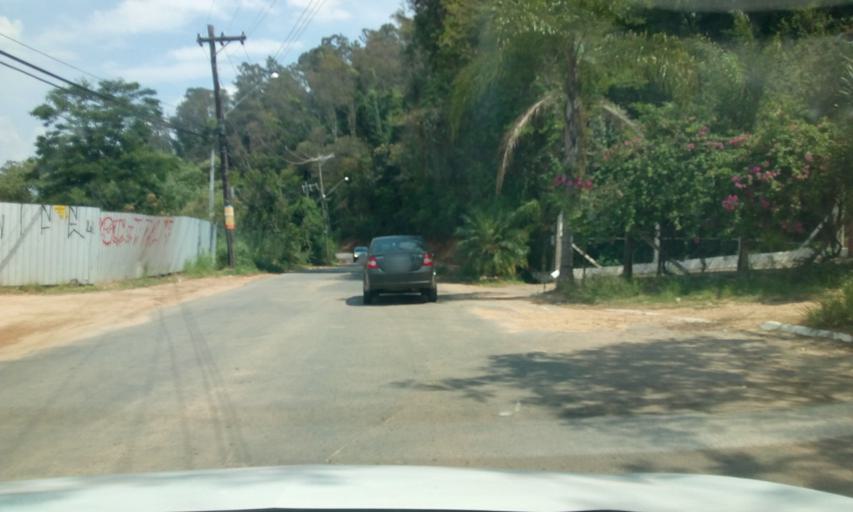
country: BR
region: Sao Paulo
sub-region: Itupeva
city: Itupeva
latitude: -23.1431
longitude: -47.0507
